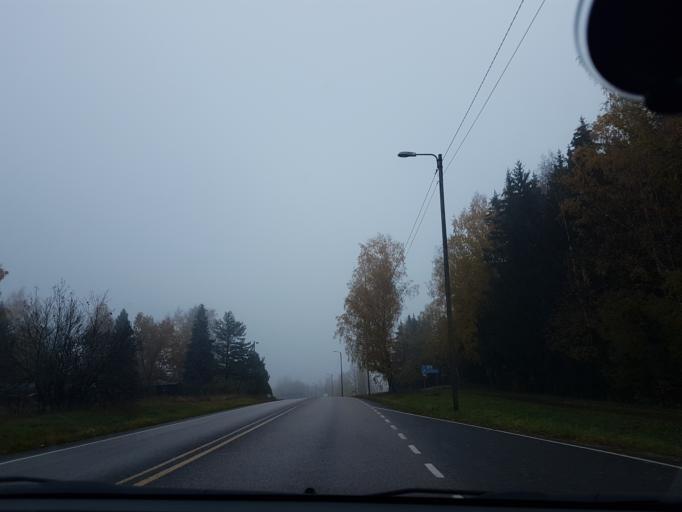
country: FI
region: Uusimaa
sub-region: Helsinki
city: Tuusula
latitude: 60.4124
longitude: 25.0474
